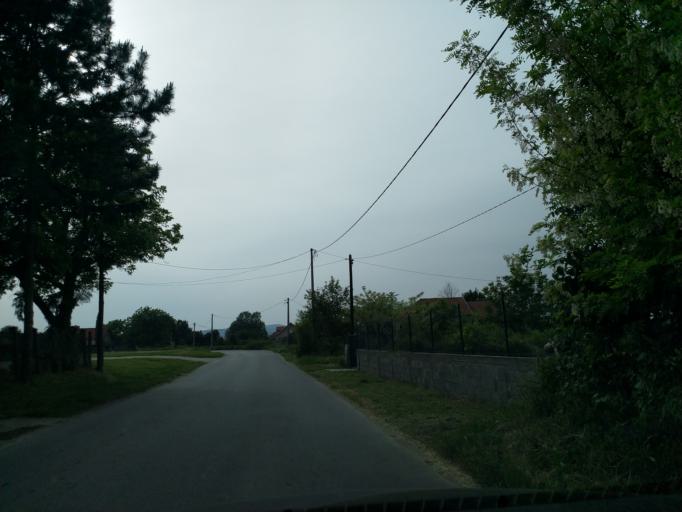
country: RS
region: Central Serbia
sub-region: Pomoravski Okrug
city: Jagodina
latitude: 43.9753
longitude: 21.2013
